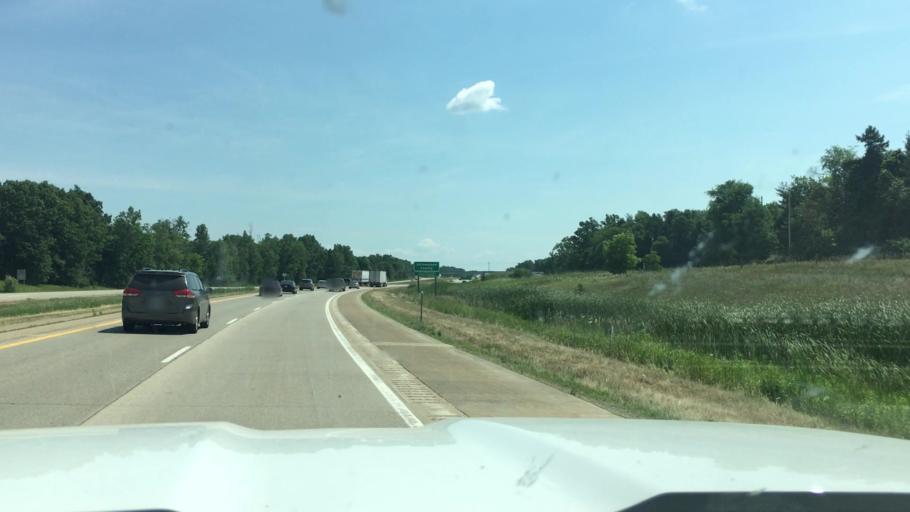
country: US
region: Michigan
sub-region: Ingham County
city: Haslett
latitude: 42.7956
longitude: -84.3646
